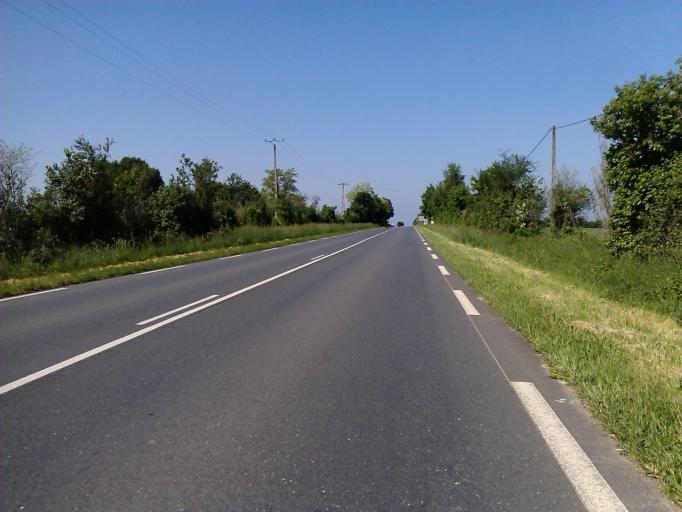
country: FR
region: Centre
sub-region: Departement de l'Indre
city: Le Pechereau
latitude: 46.6039
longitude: 1.6307
